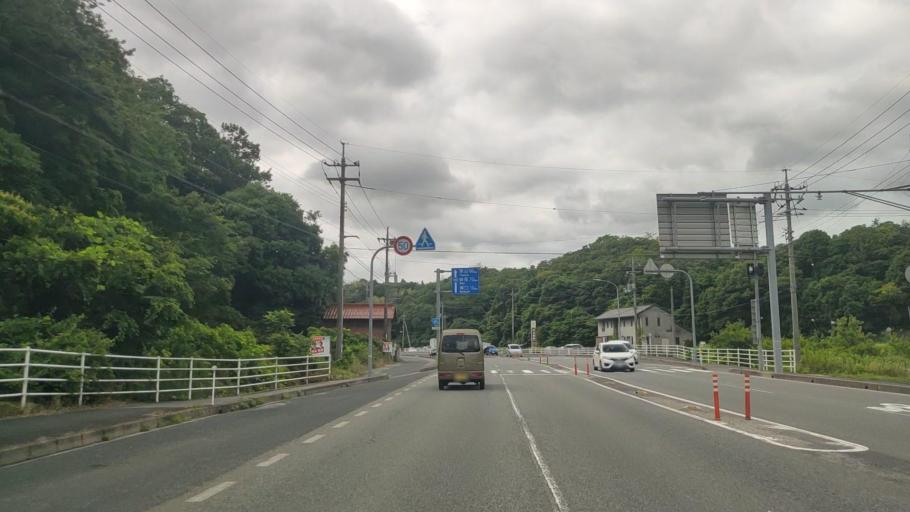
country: JP
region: Tottori
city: Yonago
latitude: 35.4153
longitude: 133.3531
